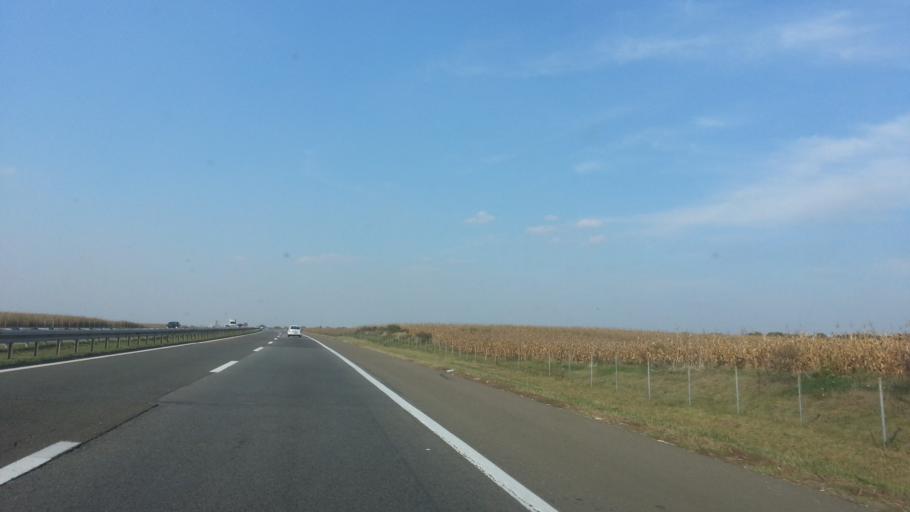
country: RS
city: Novi Banovci
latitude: 44.9208
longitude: 20.3043
